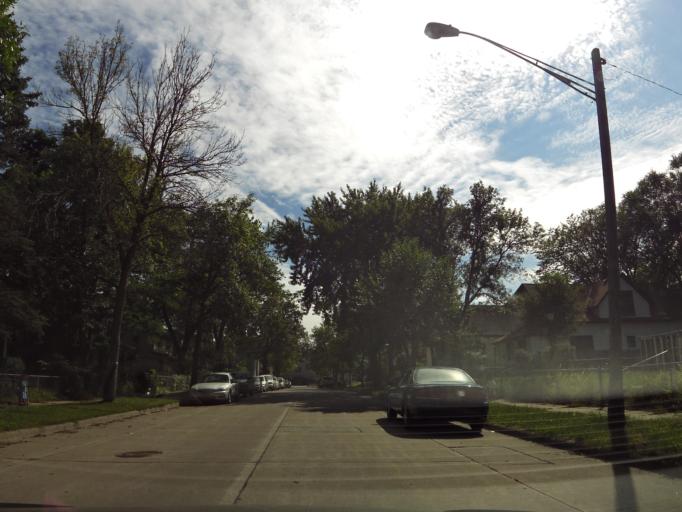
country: US
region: Minnesota
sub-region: Anoka County
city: Columbia Heights
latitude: 45.0218
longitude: -93.2461
